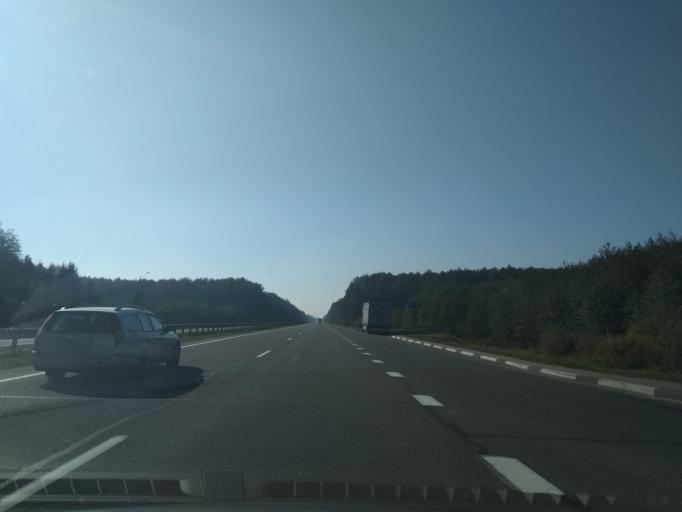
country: BY
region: Brest
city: Ivatsevichy
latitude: 52.6938
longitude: 25.3515
